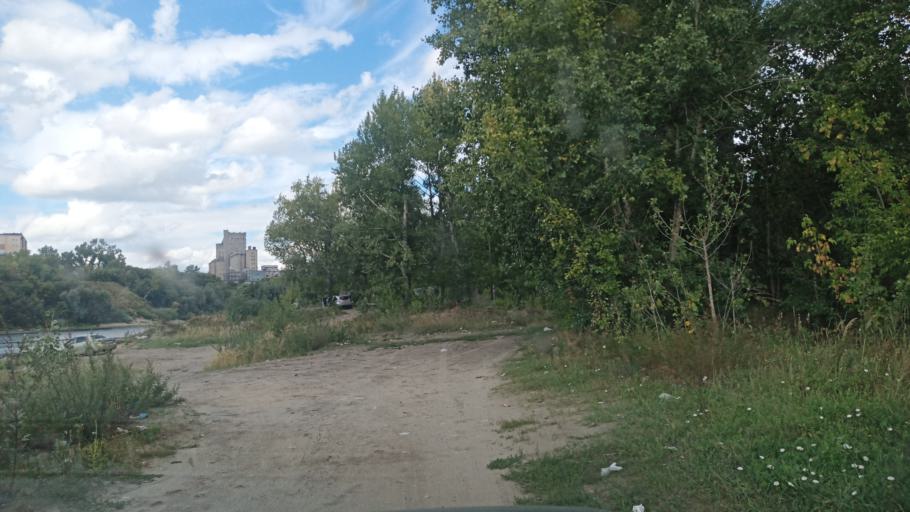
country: RU
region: Altai Krai
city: Zaton
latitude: 53.3358
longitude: 83.8061
